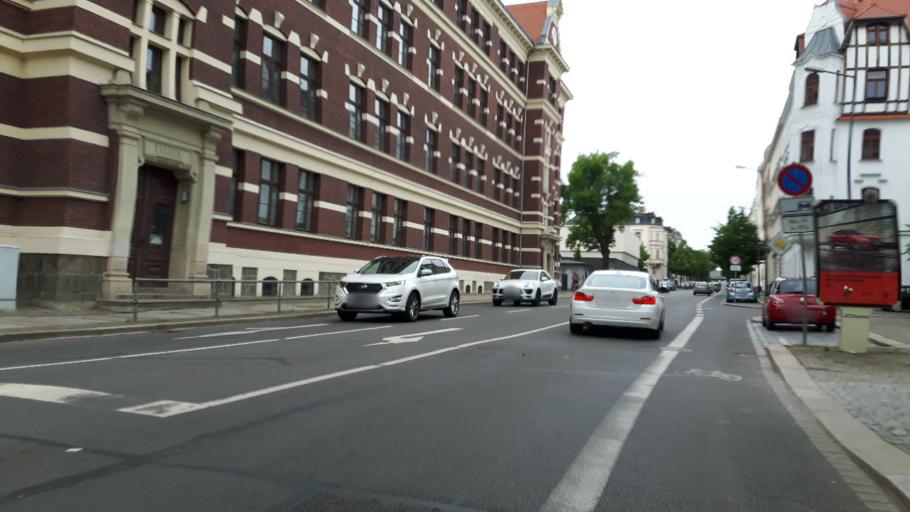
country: DE
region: Saxony
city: Leipzig
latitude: 51.3635
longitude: 12.3617
